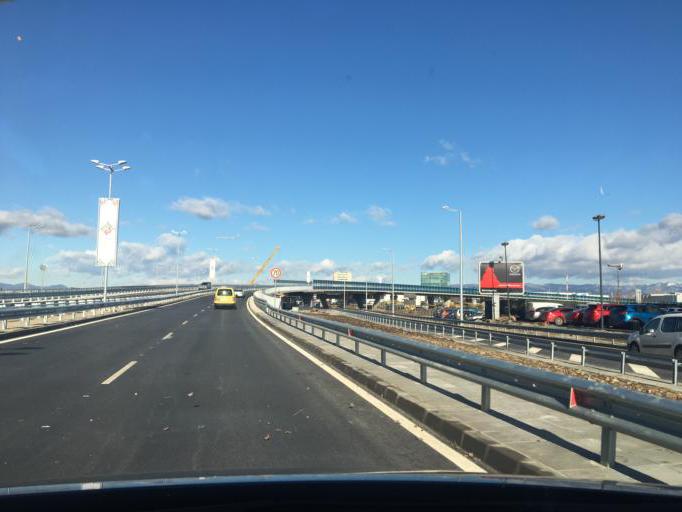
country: BG
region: Sofia-Capital
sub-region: Stolichna Obshtina
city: Sofia
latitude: 42.6804
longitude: 23.3990
